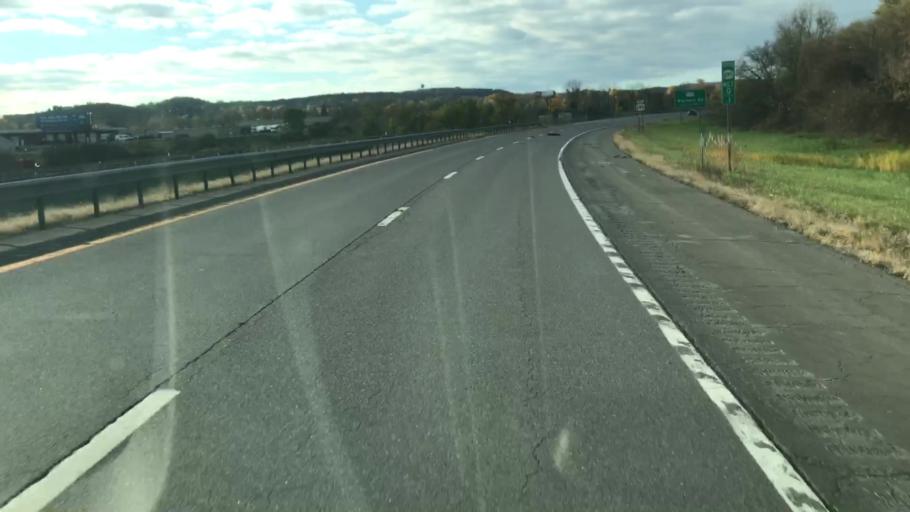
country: US
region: New York
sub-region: Onondaga County
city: Fairmount
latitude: 43.0566
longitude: -76.2383
